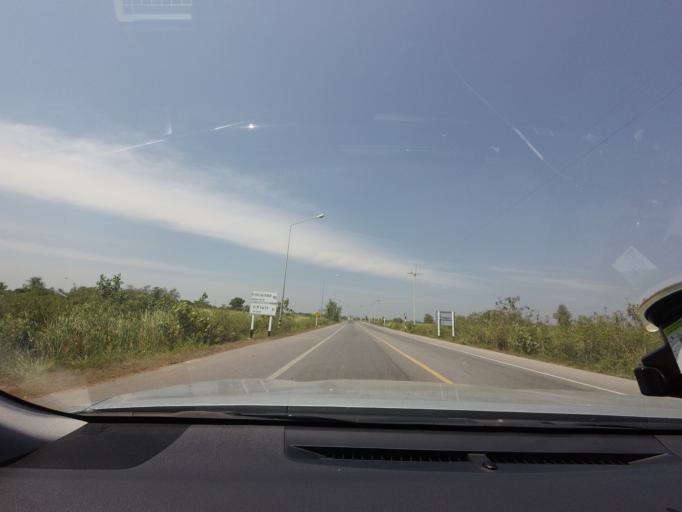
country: TH
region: Surat Thani
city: Tha Chang
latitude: 9.2219
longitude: 99.2189
